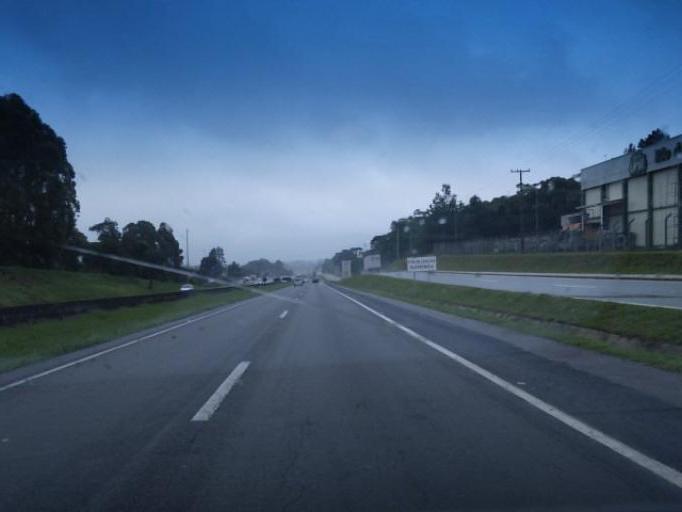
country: BR
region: Parana
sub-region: Sao Jose Dos Pinhais
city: Sao Jose dos Pinhais
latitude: -25.7139
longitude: -49.1390
